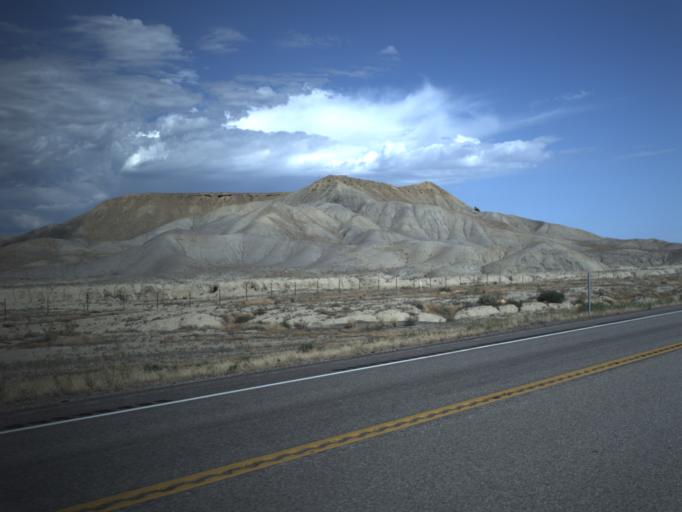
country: US
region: Utah
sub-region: Carbon County
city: East Carbon City
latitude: 39.2866
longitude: -110.3511
